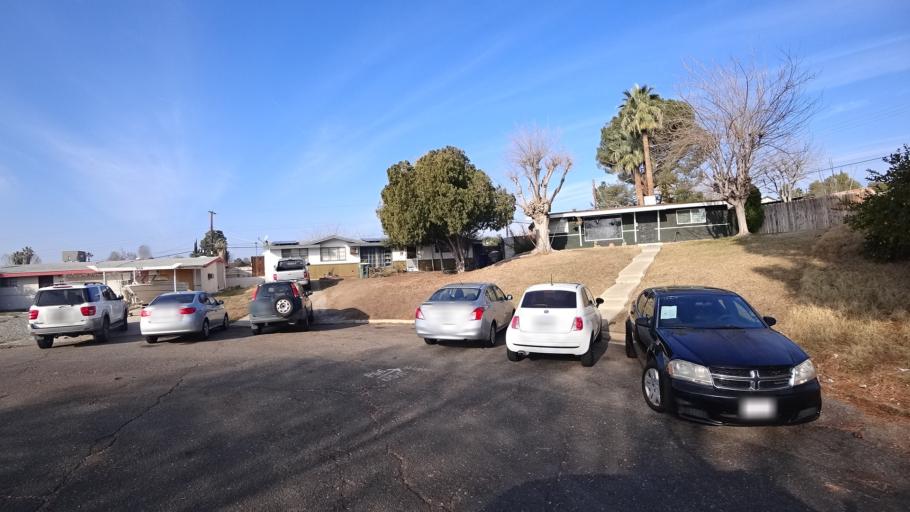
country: US
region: California
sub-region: Kern County
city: Oildale
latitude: 35.4032
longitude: -118.9841
